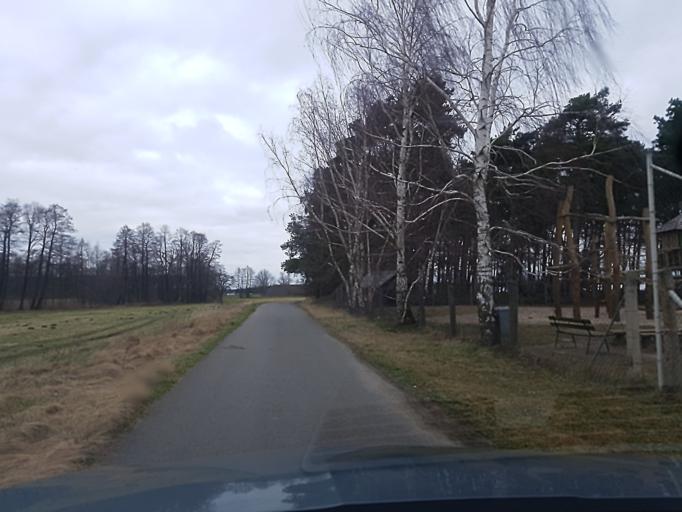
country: DE
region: Brandenburg
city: Bad Liebenwerda
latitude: 51.5489
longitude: 13.3537
